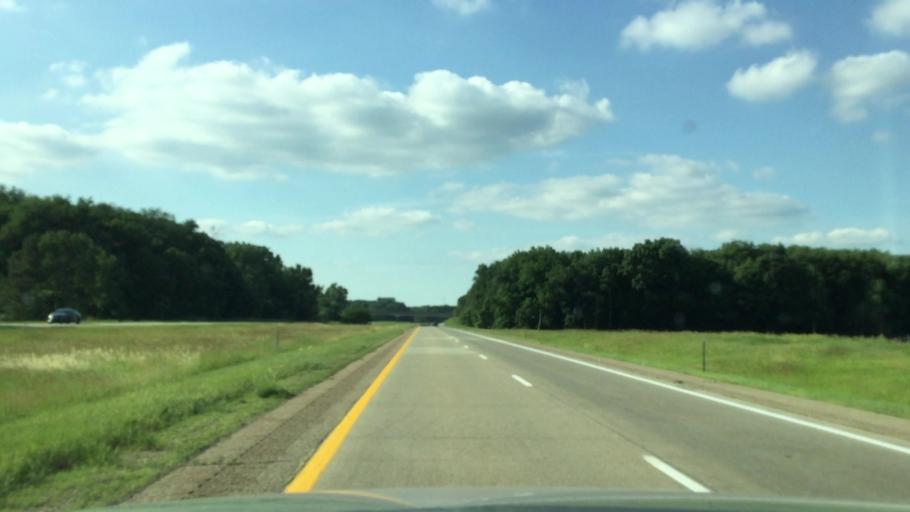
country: US
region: Michigan
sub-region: Calhoun County
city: Marshall
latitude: 42.1261
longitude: -84.9953
